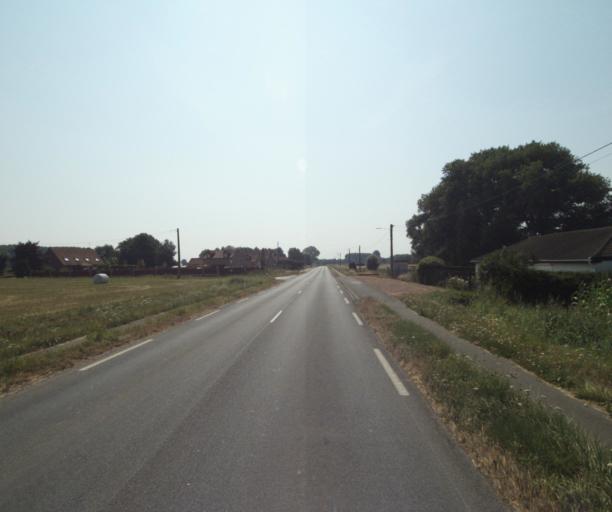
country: FR
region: Nord-Pas-de-Calais
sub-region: Departement du Nord
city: Quesnoy-sur-Deule
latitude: 50.7052
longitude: 3.0153
